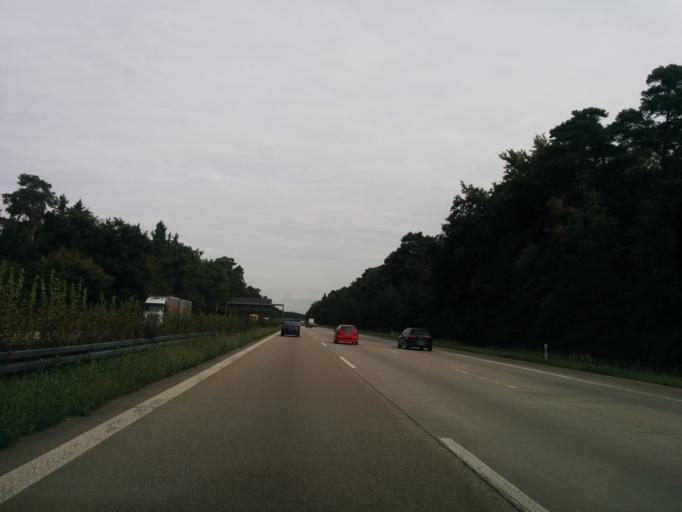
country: DE
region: Baden-Wuerttemberg
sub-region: Karlsruhe Region
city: Kronau
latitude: 49.2371
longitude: 8.6020
